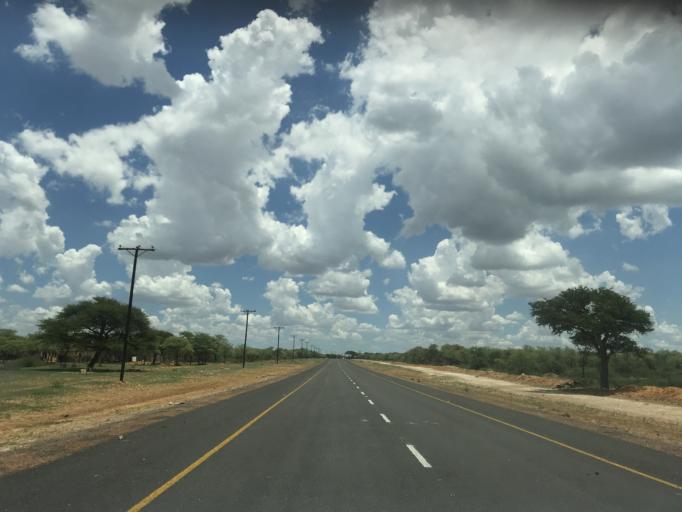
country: BW
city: Mabuli
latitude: -25.8040
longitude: 24.8235
